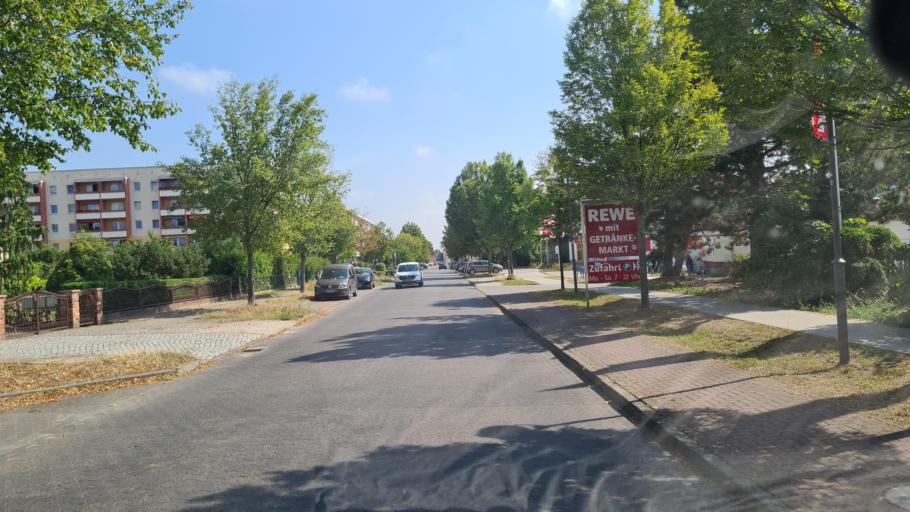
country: DE
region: Brandenburg
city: Beelitz
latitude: 52.2390
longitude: 12.9724
